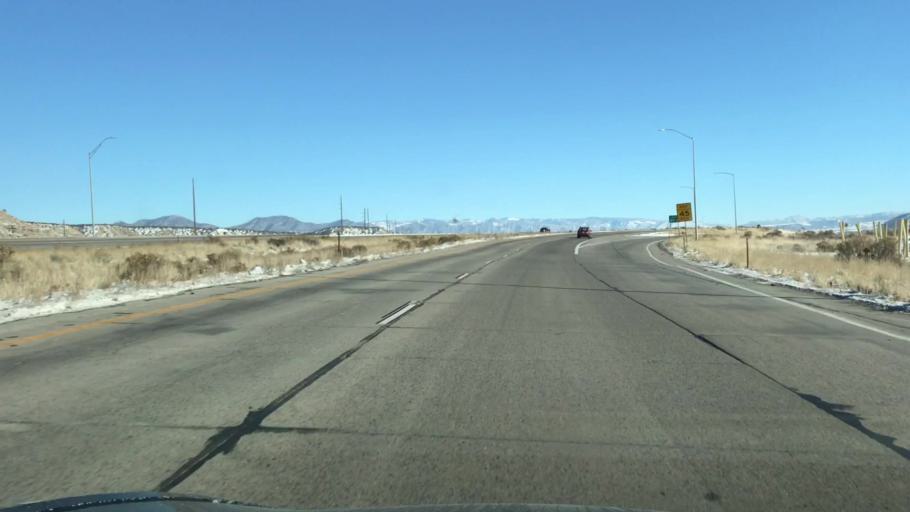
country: US
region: Colorado
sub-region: Garfield County
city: Rifle
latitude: 39.5215
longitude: -107.8510
